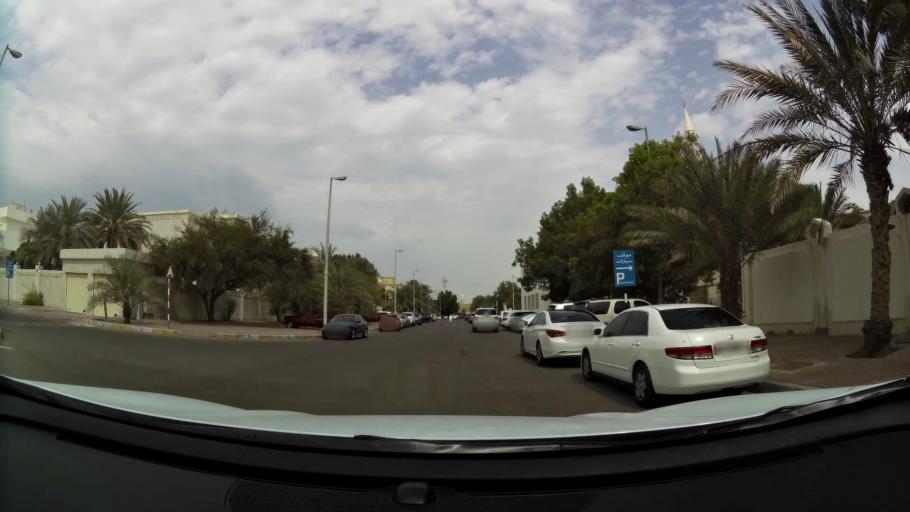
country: AE
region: Abu Dhabi
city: Abu Dhabi
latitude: 24.4576
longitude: 54.3436
